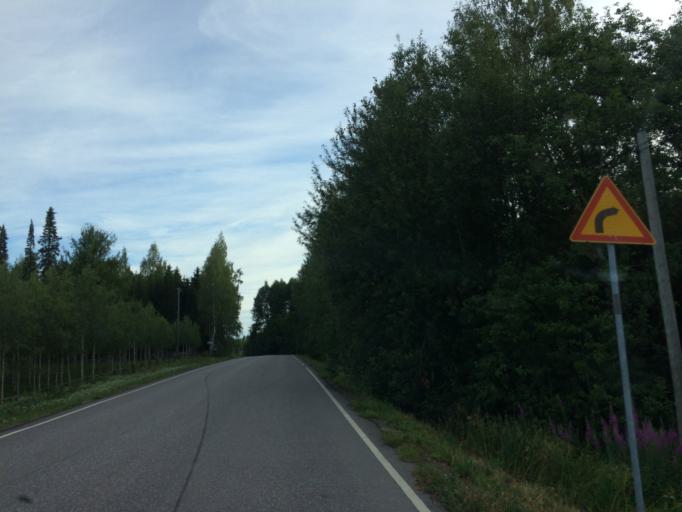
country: FI
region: Haeme
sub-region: Haemeenlinna
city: Janakkala
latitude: 60.8762
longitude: 24.5645
